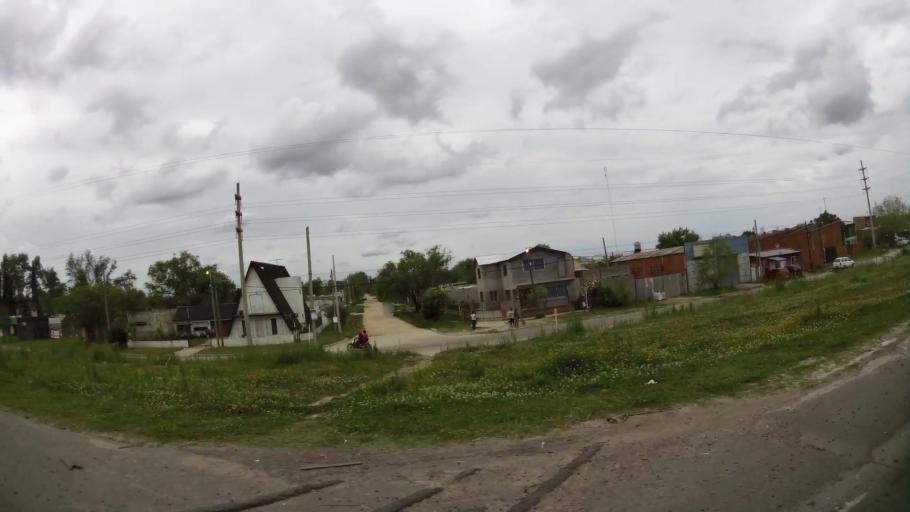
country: AR
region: Buenos Aires
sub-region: Partido de Zarate
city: Zarate
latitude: -34.1387
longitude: -59.0078
